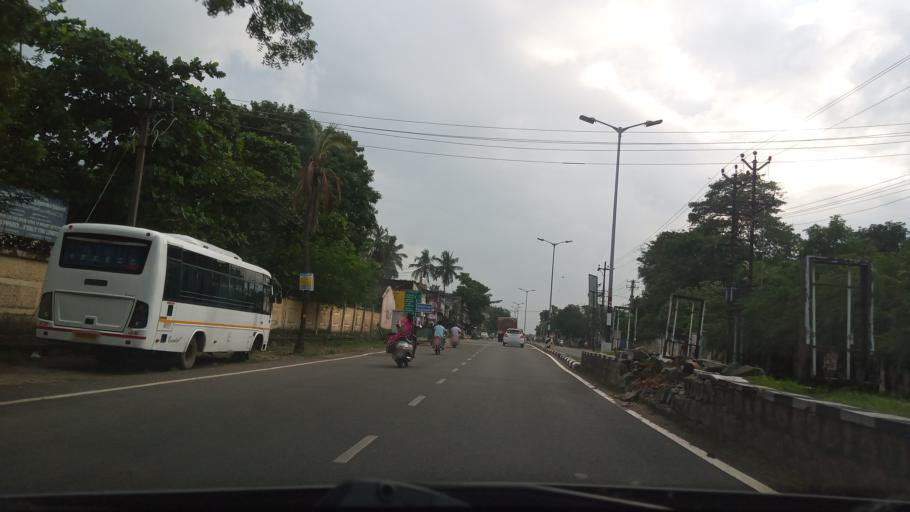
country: IN
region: Tamil Nadu
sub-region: Villupuram
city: Auroville
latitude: 12.0099
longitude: 79.8566
